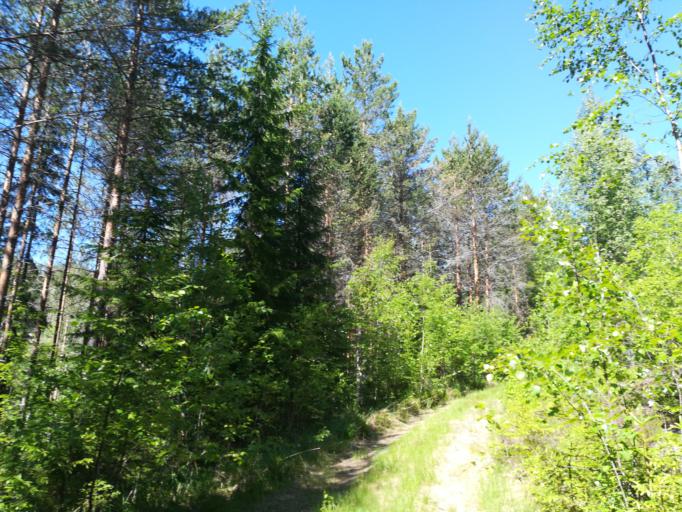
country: FI
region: Southern Savonia
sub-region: Mikkeli
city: Puumala
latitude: 61.6172
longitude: 28.1618
